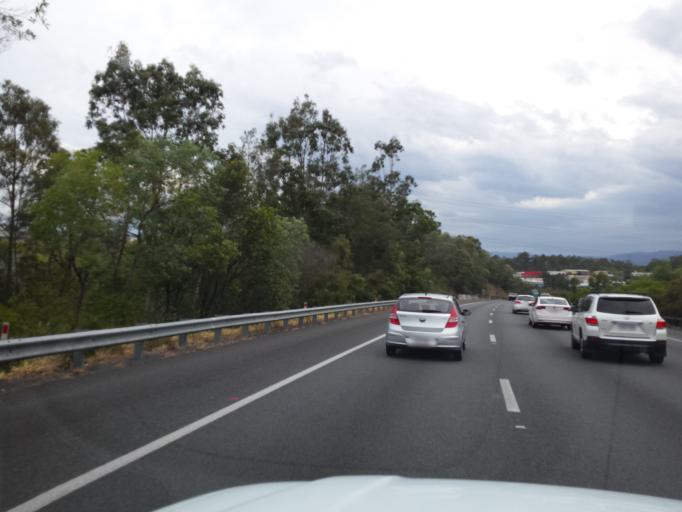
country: AU
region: Queensland
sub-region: Gold Coast
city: Nerang
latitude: -27.9751
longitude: 153.3459
